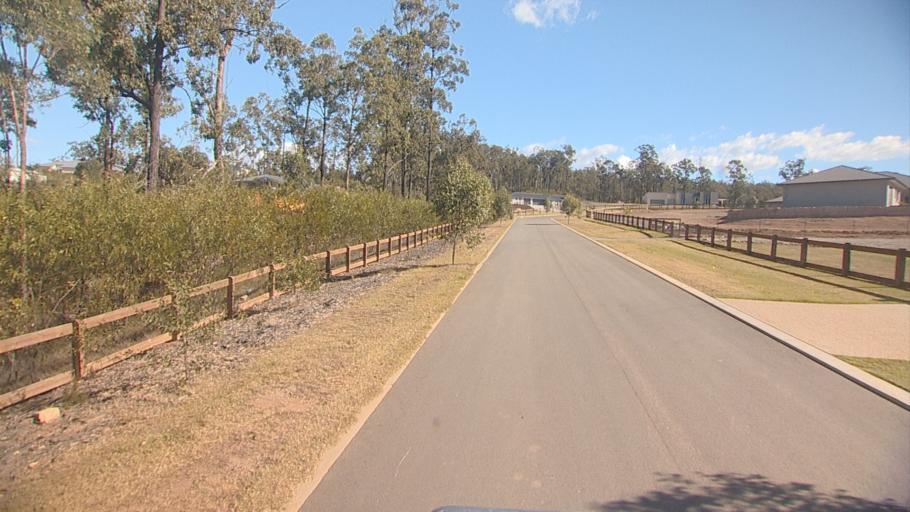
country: AU
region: Queensland
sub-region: Ipswich
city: Springfield Lakes
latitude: -27.7316
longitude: 152.9046
